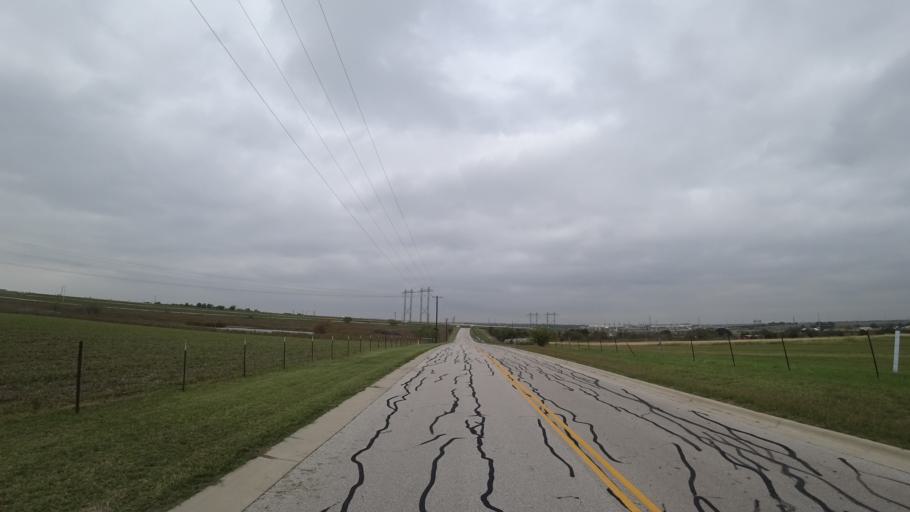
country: US
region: Texas
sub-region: Travis County
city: Pflugerville
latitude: 30.4034
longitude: -97.5787
